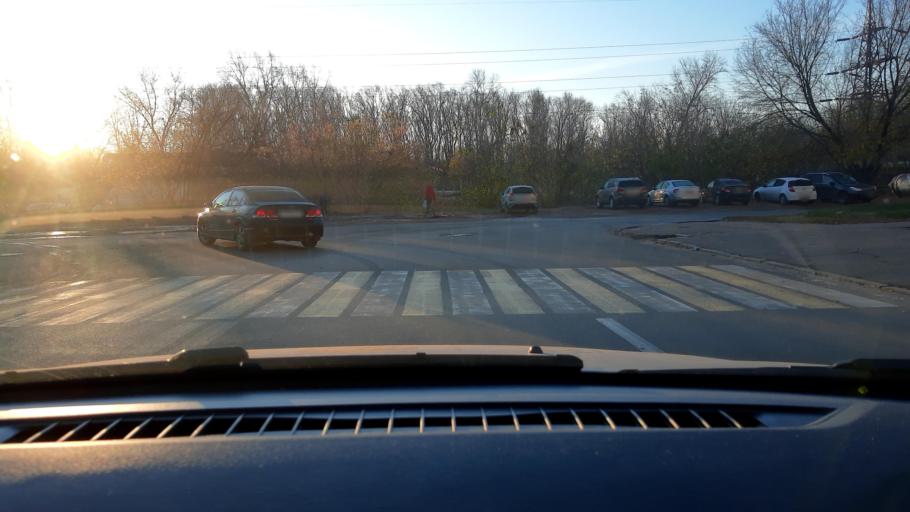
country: RU
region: Nizjnij Novgorod
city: Burevestnik
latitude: 56.2275
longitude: 43.8807
